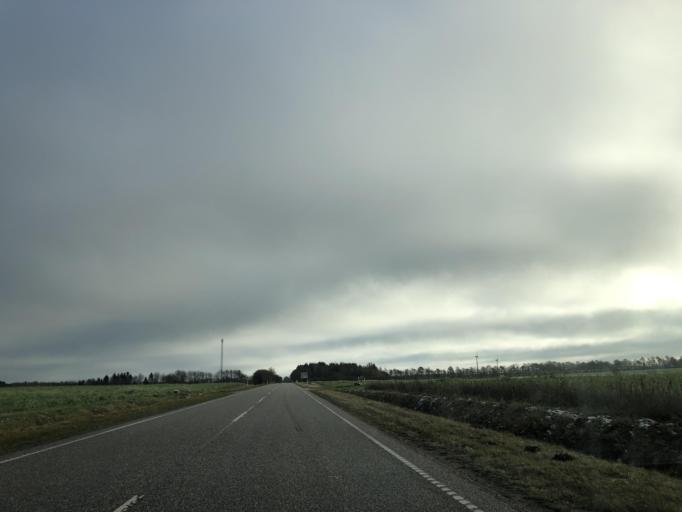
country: DK
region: Central Jutland
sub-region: Horsens Kommune
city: Braedstrup
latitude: 55.9126
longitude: 9.5762
